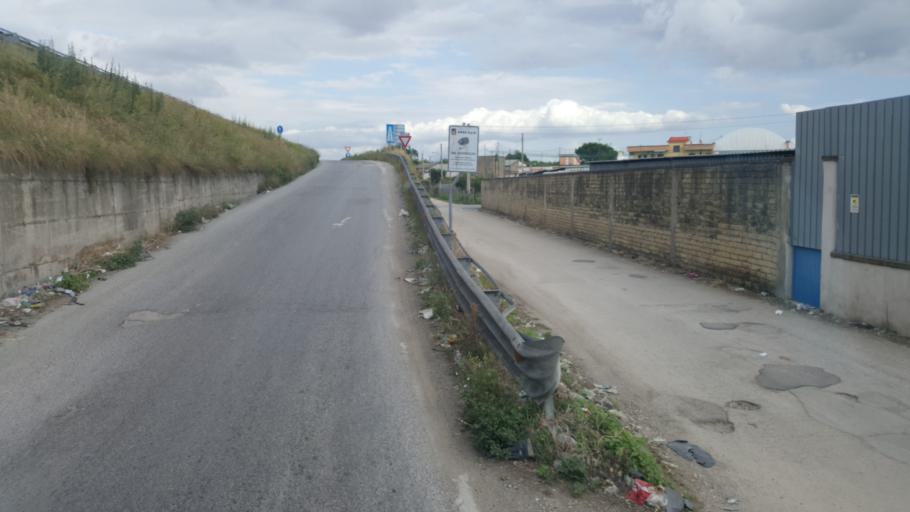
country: IT
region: Campania
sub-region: Provincia di Napoli
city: Acerra
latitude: 40.9647
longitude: 14.3732
